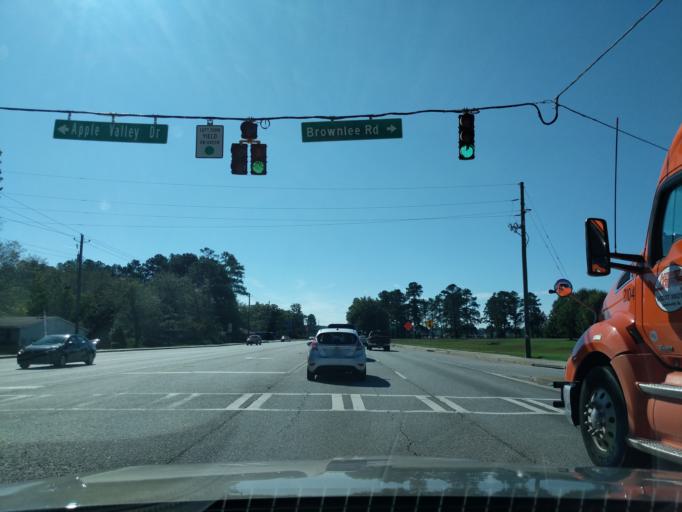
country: US
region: Georgia
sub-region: Richmond County
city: Augusta
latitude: 33.3983
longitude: -82.0056
